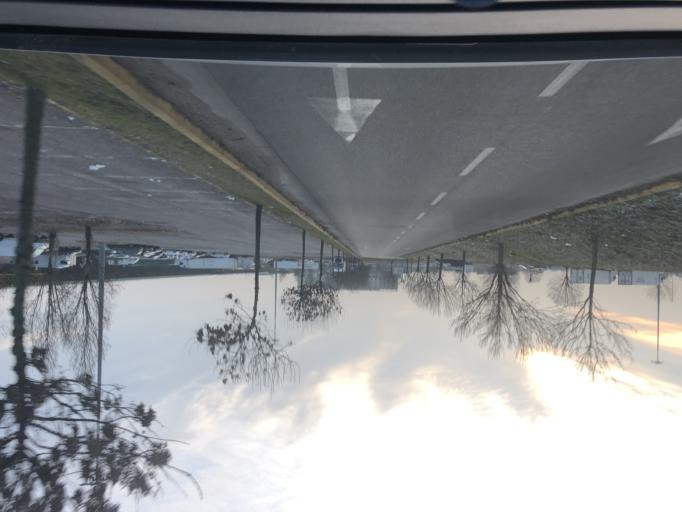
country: IT
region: Veneto
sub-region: Provincia di Verona
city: Dossobuono
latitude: 45.4134
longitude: 10.9203
